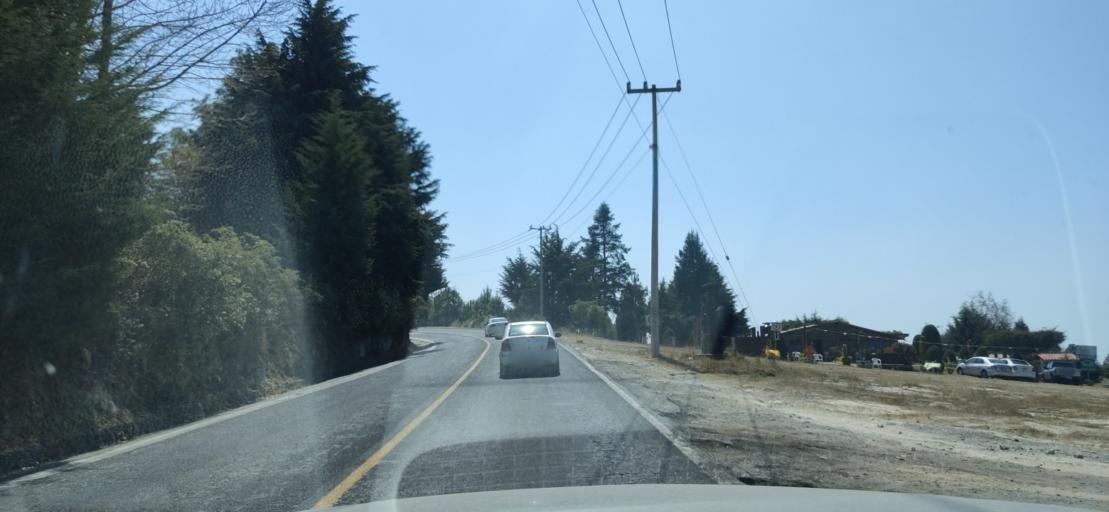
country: MX
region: Mexico
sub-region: Ocoyoacac
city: San Jeronimo Acazulco
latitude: 19.2656
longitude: -99.3766
